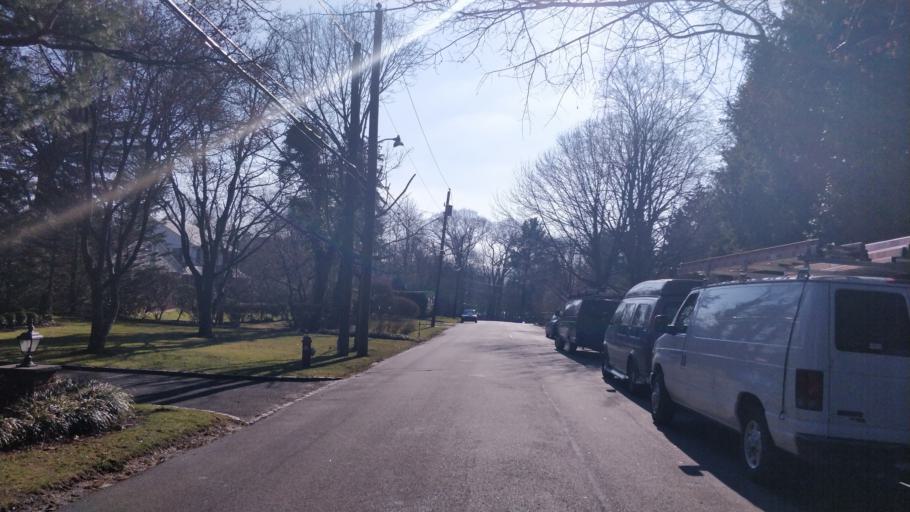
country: US
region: New York
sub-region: Nassau County
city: Sea Cliff
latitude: 40.8411
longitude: -73.6440
